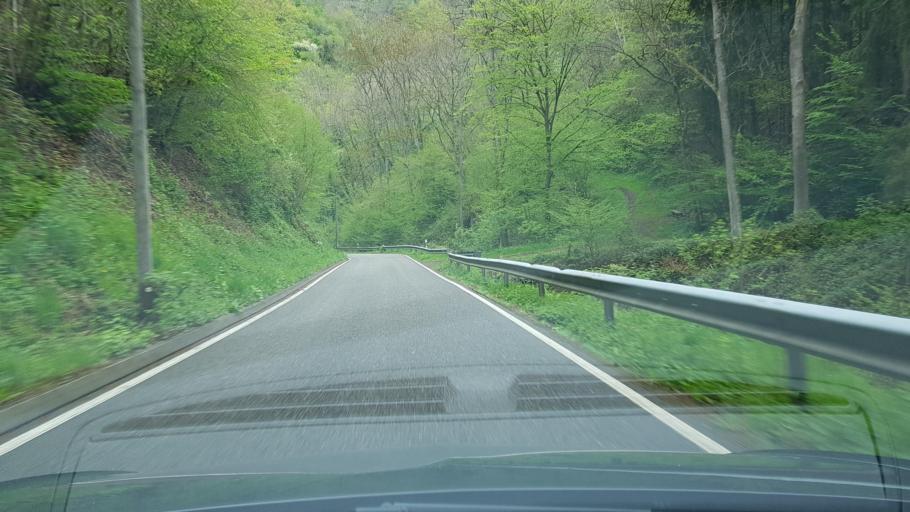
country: DE
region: Rheinland-Pfalz
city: Alken
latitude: 50.2565
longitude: 7.4575
